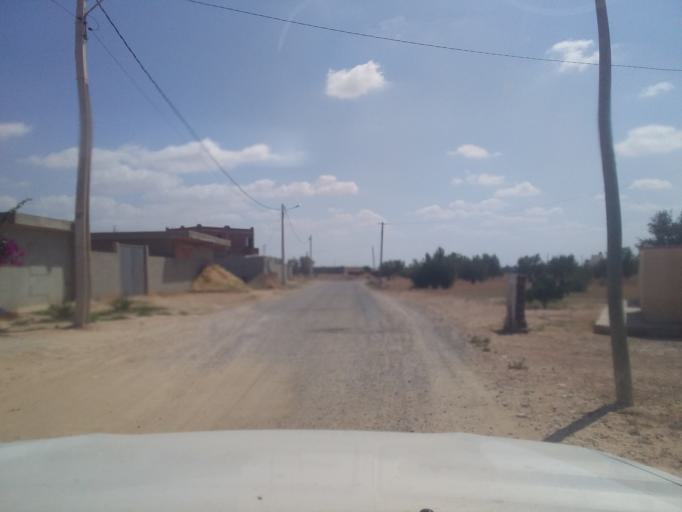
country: TN
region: Madanin
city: Medenine
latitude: 33.6122
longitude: 10.3032
